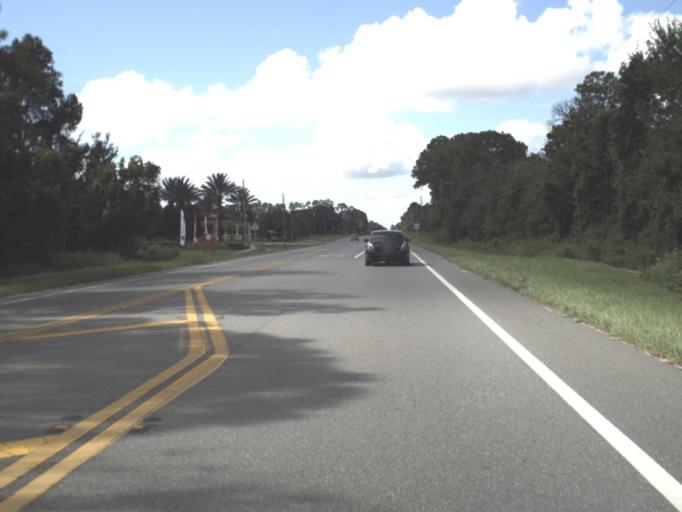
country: US
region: Florida
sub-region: Polk County
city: Loughman
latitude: 28.2166
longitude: -81.5716
